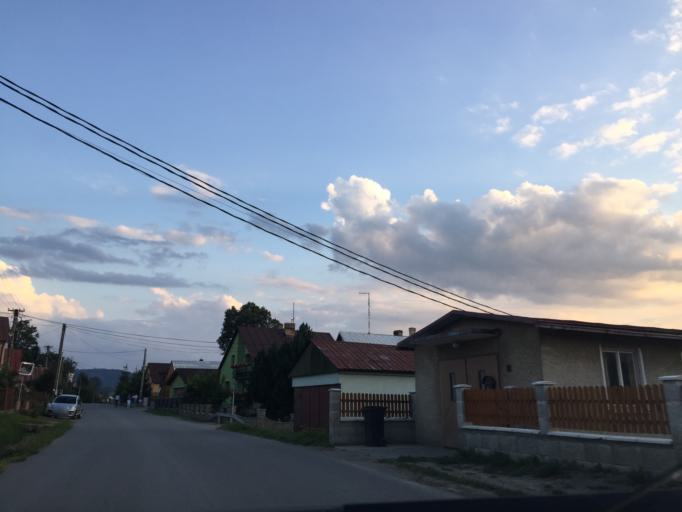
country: PL
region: Silesian Voivodeship
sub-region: Powiat zywiecki
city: Korbielow
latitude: 49.4768
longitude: 19.3828
